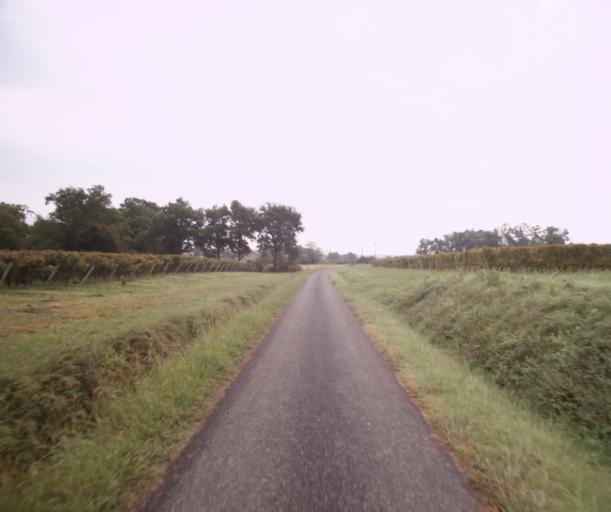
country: FR
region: Midi-Pyrenees
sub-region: Departement du Gers
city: Cazaubon
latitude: 43.9179
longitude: -0.1273
